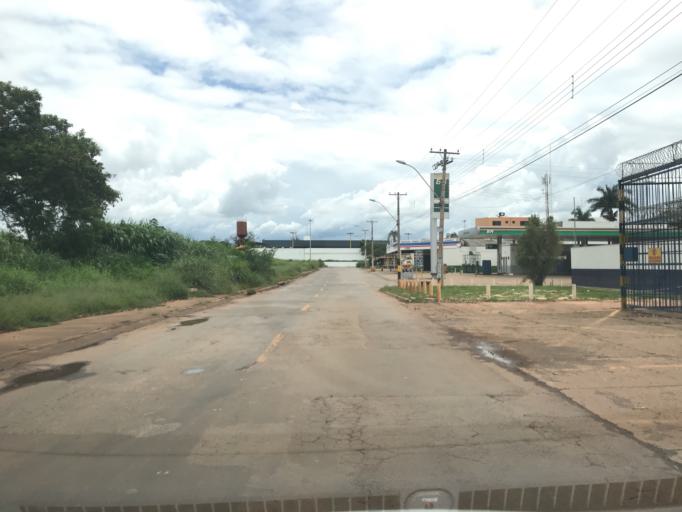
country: BR
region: Federal District
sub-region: Brasilia
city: Brasilia
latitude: -15.8178
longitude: -47.9571
